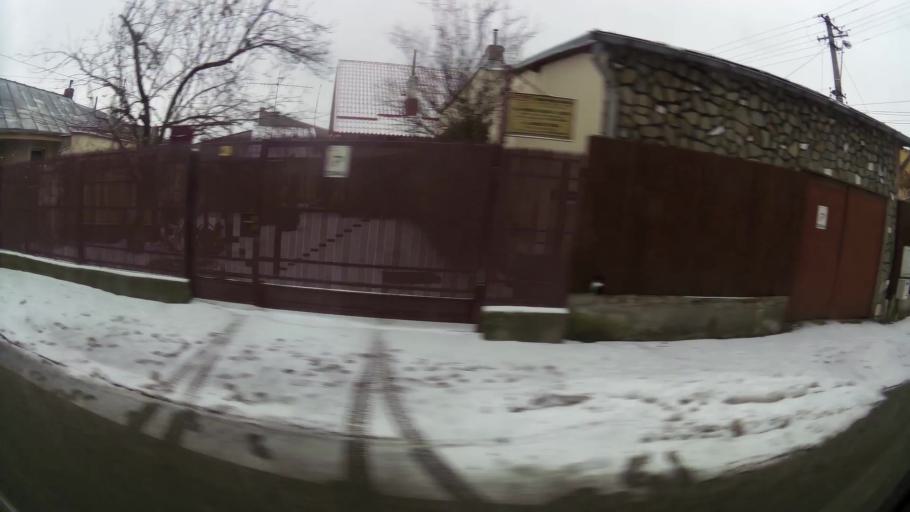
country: RO
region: Prahova
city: Ploiesti
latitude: 44.9329
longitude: 26.0450
